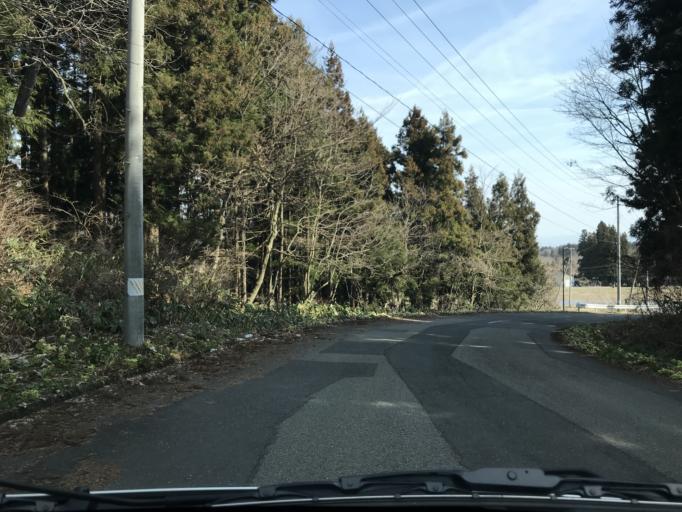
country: JP
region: Iwate
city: Mizusawa
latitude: 39.1183
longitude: 141.0121
